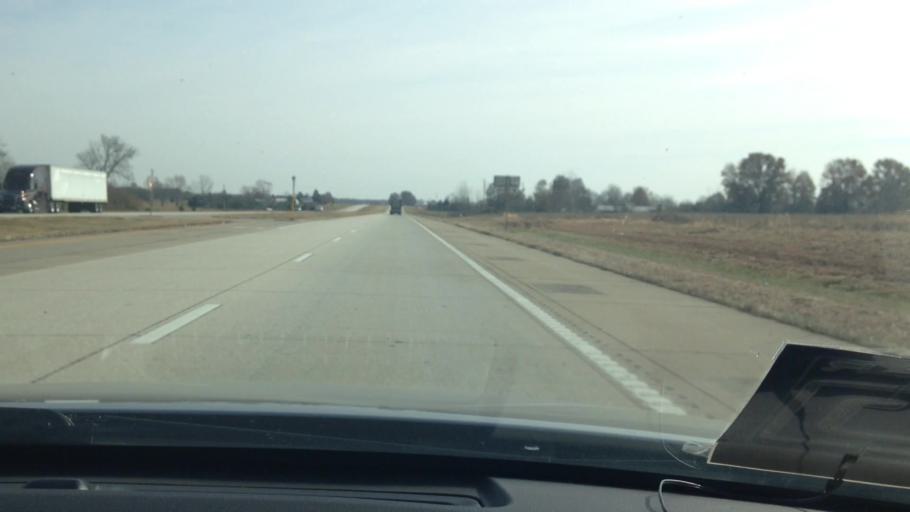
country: US
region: Missouri
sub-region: Henry County
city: Clinton
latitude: 38.4345
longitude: -93.9346
